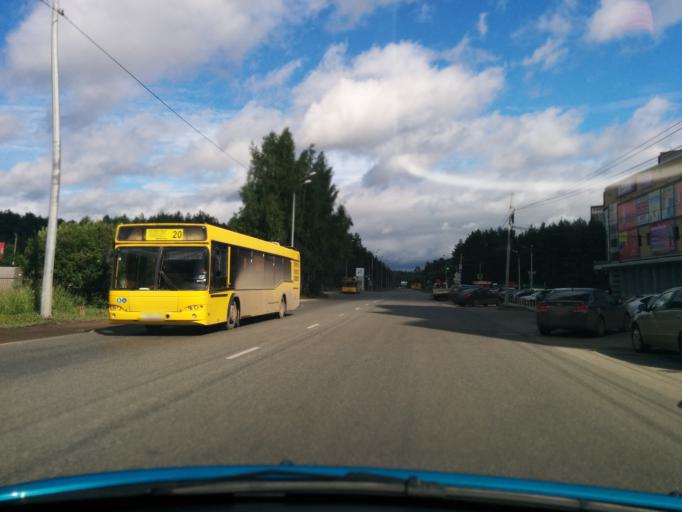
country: RU
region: Perm
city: Kondratovo
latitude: 58.0363
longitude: 56.1433
